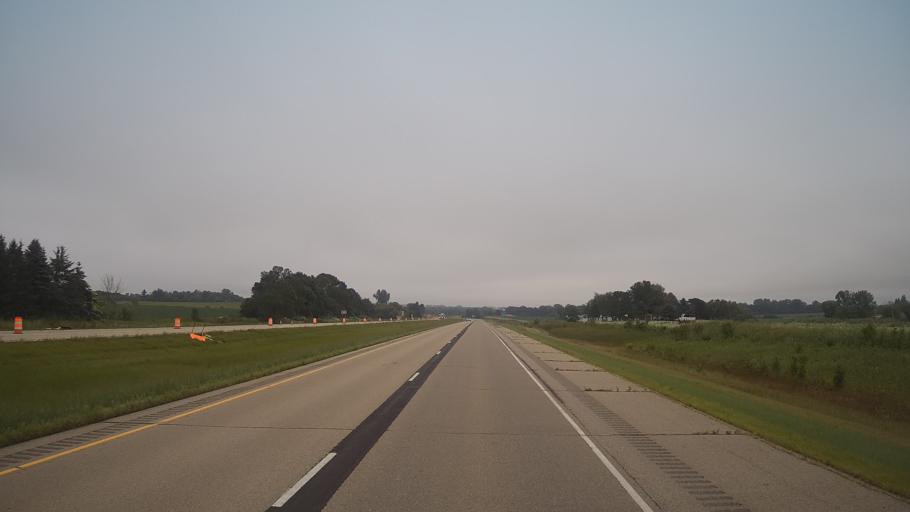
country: US
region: Minnesota
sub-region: Olmsted County
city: Stewartville
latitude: 43.8322
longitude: -92.5552
